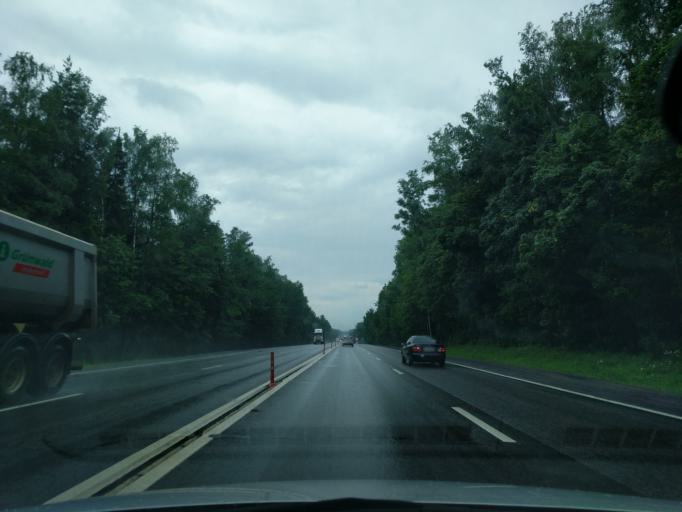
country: RU
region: Moskovskaya
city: Kievskij
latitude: 55.4093
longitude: 36.8252
